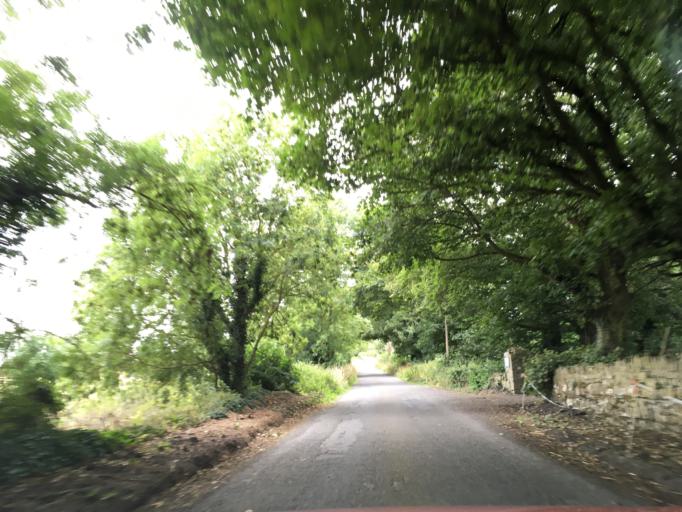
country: IE
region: Munster
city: Cashel
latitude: 52.4735
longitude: -7.9114
